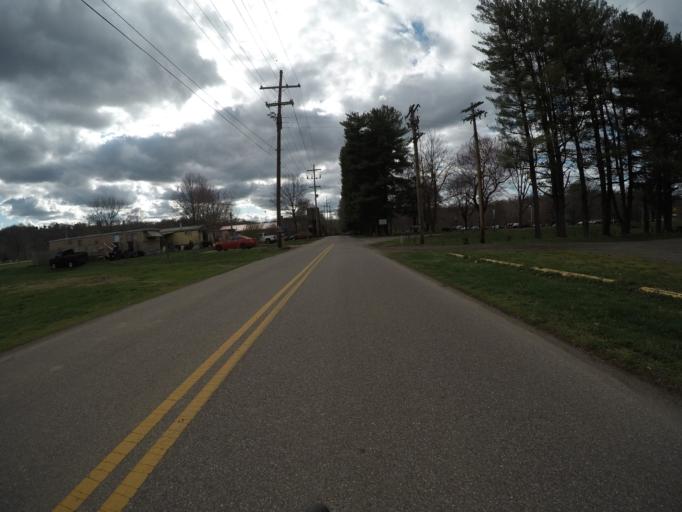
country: US
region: Ohio
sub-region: Washington County
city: Marietta
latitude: 39.4318
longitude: -81.4684
